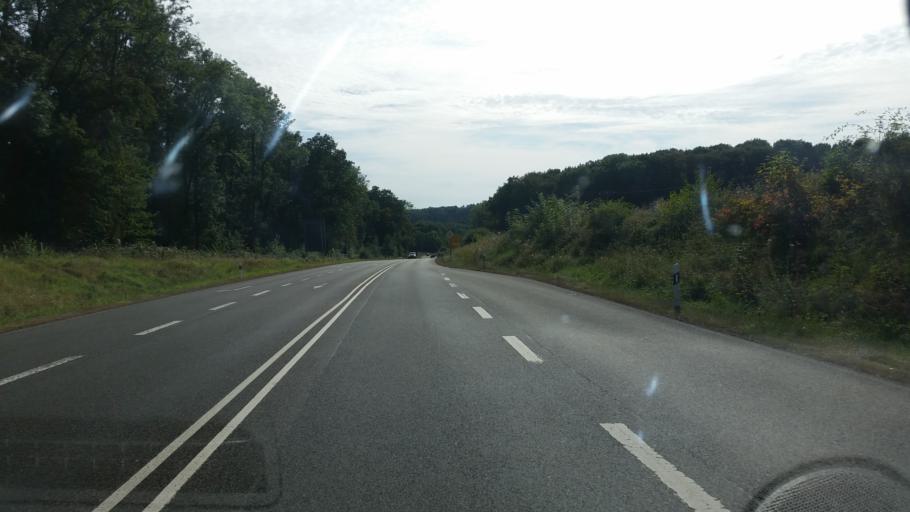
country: DE
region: Rheinland-Pfalz
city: Neuhausel
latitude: 50.3756
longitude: 7.6987
